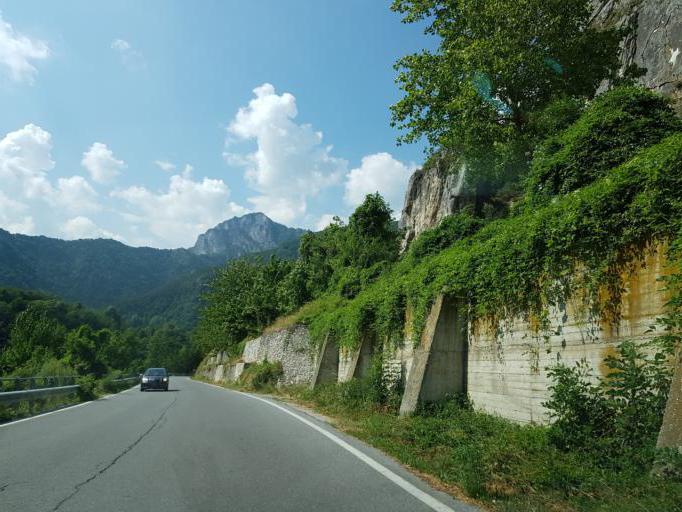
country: IT
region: Piedmont
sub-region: Provincia di Cuneo
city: San Damiano Macra
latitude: 44.4889
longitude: 7.2456
